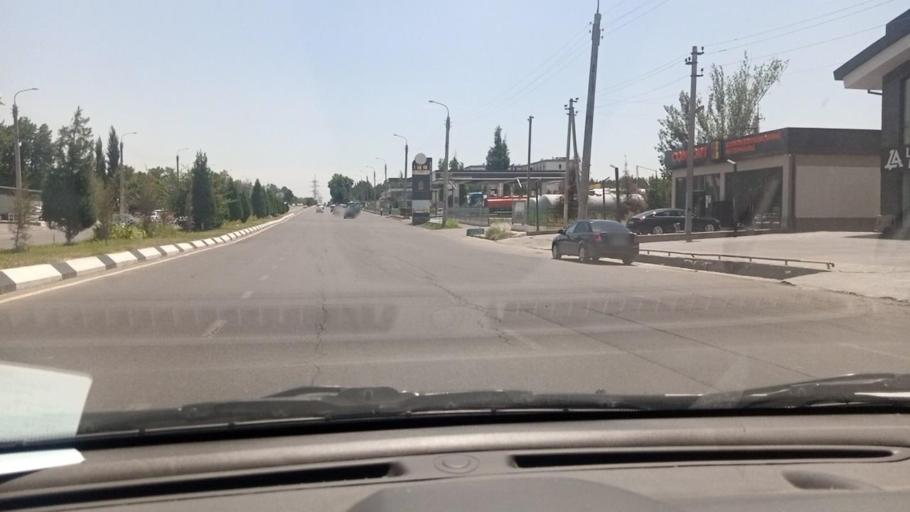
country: UZ
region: Toshkent Shahri
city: Tashkent
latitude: 41.3050
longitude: 69.1936
